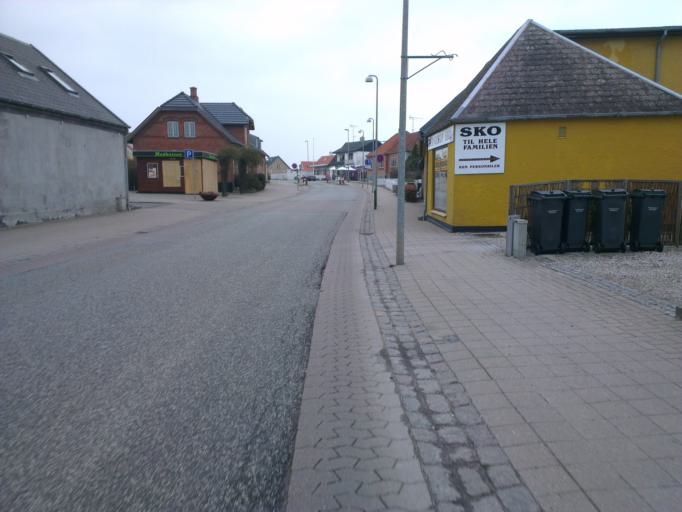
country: DK
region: Capital Region
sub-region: Frederikssund Kommune
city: Slangerup
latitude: 55.8474
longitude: 12.1722
